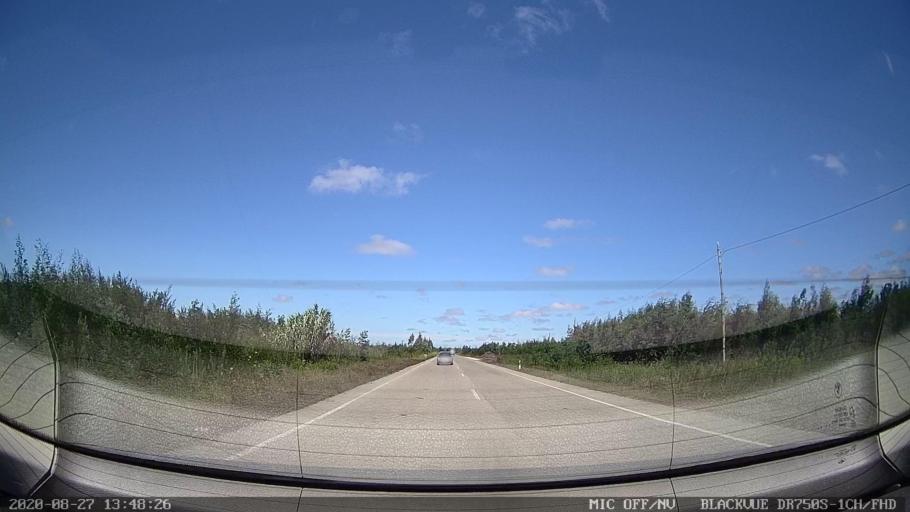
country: PT
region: Coimbra
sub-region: Mira
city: Mira
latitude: 40.3778
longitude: -8.7449
